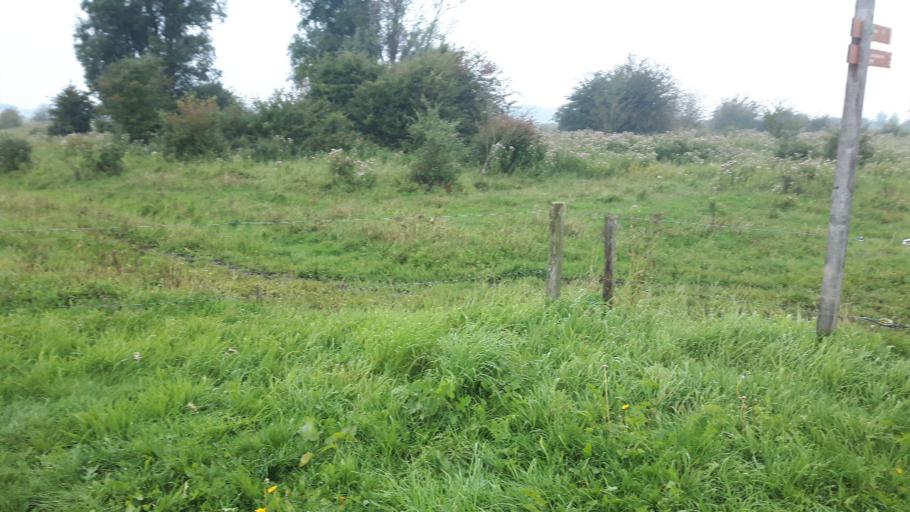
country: NL
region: Friesland
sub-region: Gemeente Kollumerland en Nieuwkruisland
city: Kollum
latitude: 53.3225
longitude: 6.2044
